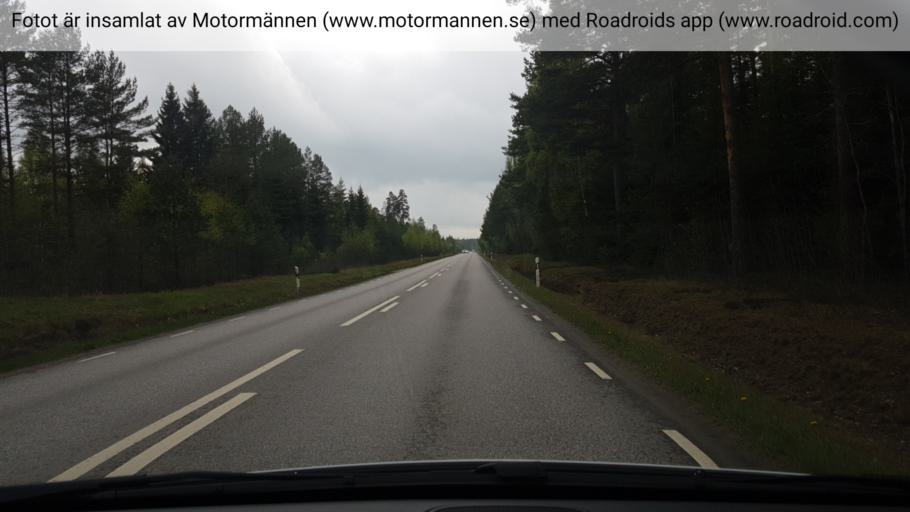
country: SE
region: Vaestra Goetaland
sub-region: Skovde Kommun
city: Stopen
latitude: 58.4519
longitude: 13.9523
